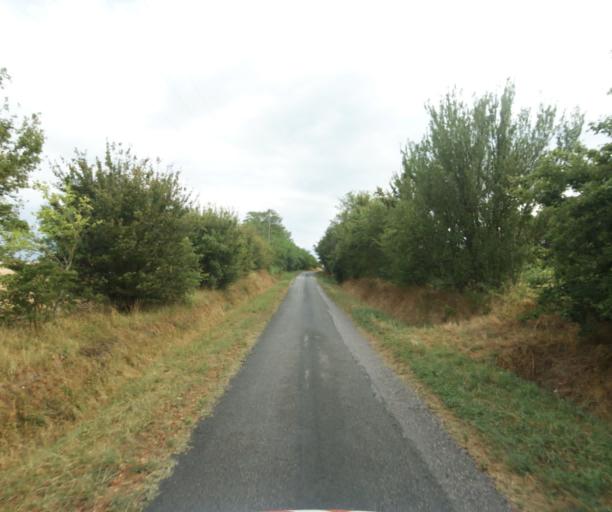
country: FR
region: Midi-Pyrenees
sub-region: Departement de la Haute-Garonne
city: Revel
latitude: 43.4266
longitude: 1.9627
